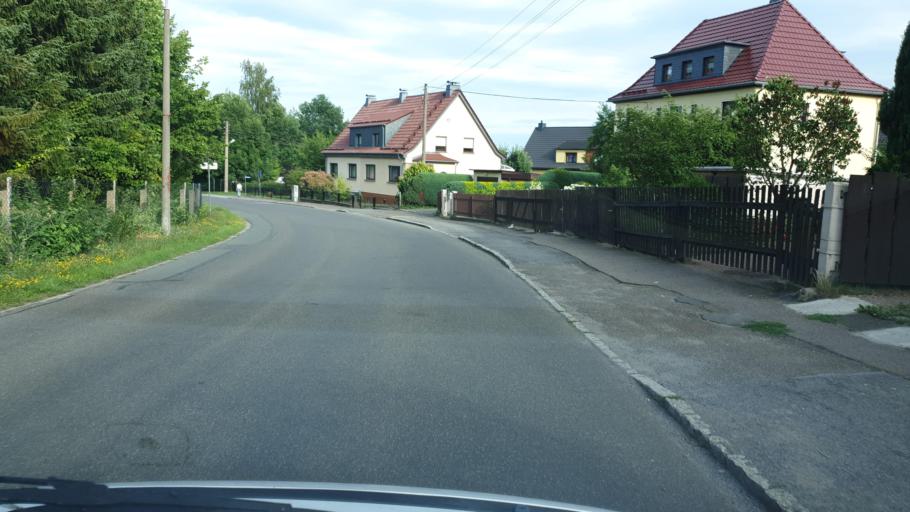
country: DE
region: Saxony
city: Hohenstein-Ernstthal
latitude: 50.8008
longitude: 12.7304
